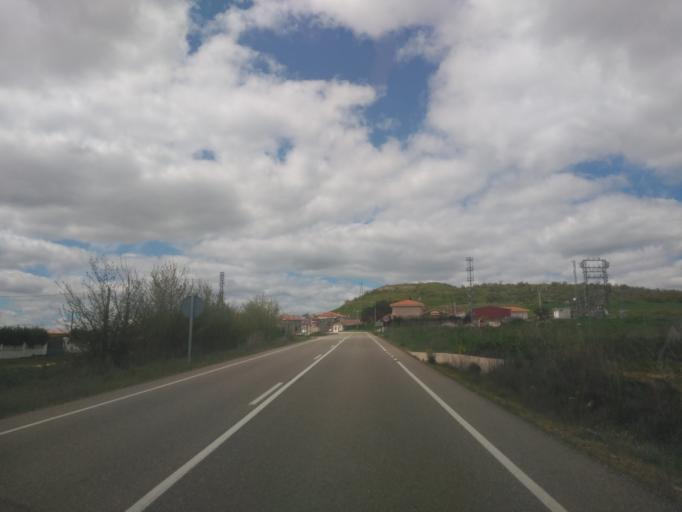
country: ES
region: Castille and Leon
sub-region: Provincia de Salamanca
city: Almenara de Tormes
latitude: 41.0630
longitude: -5.8179
